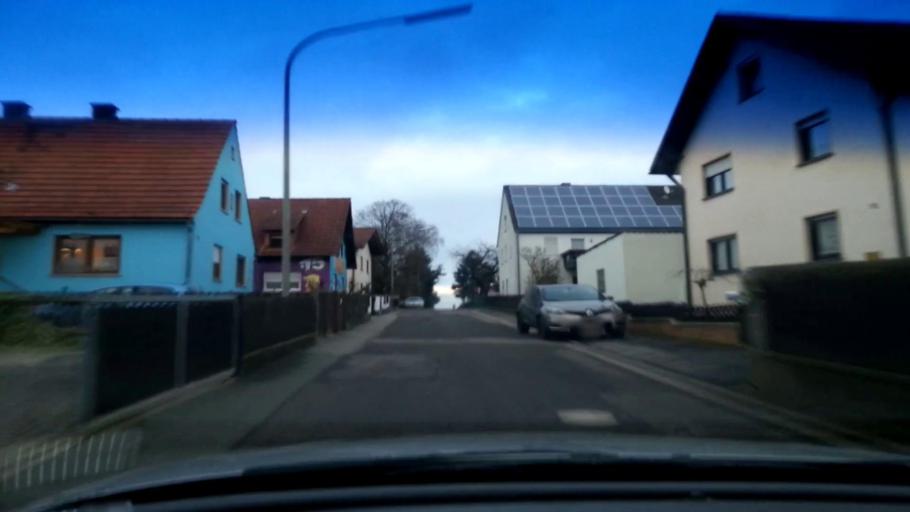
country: DE
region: Bavaria
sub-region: Upper Franconia
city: Viereth-Trunstadt
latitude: 49.9037
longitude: 10.7722
